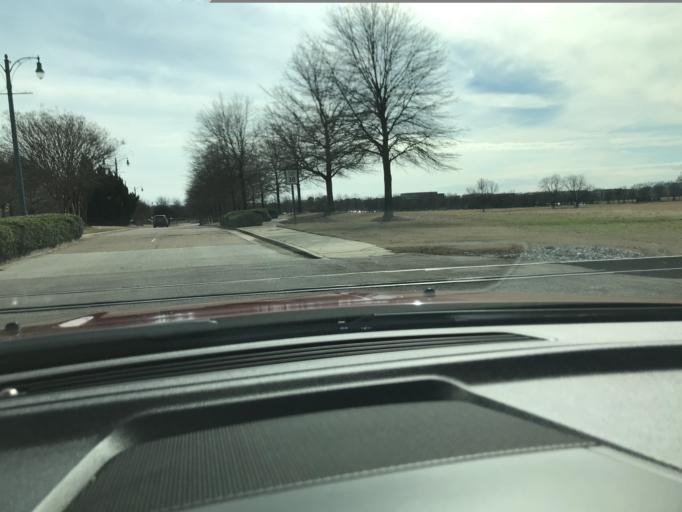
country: US
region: Tennessee
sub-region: Shelby County
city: Collierville
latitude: 35.0459
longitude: -89.7007
